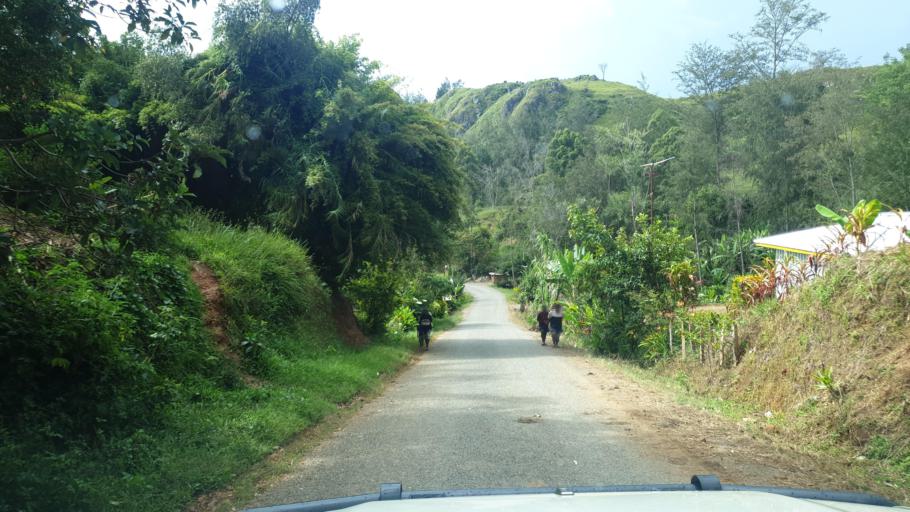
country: PG
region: Chimbu
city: Kundiawa
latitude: -6.1583
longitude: 145.1343
